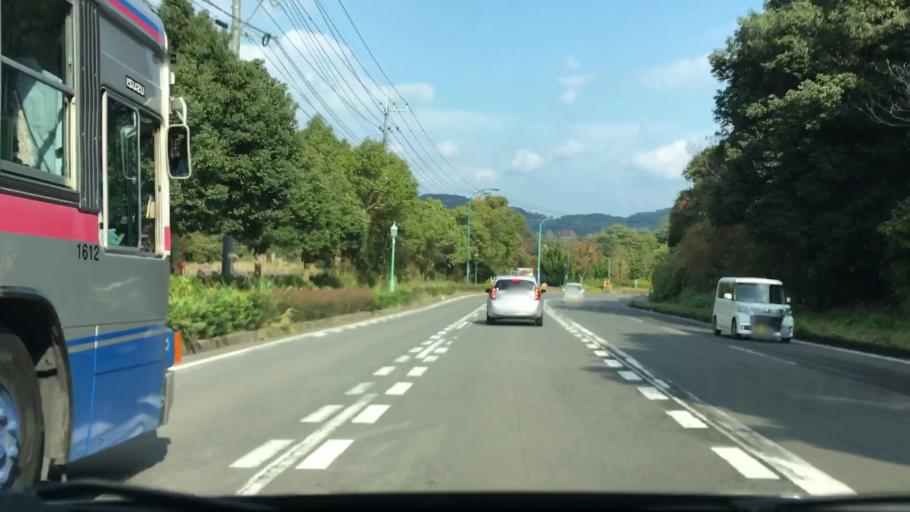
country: JP
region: Nagasaki
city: Sasebo
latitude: 32.9940
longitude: 129.7520
